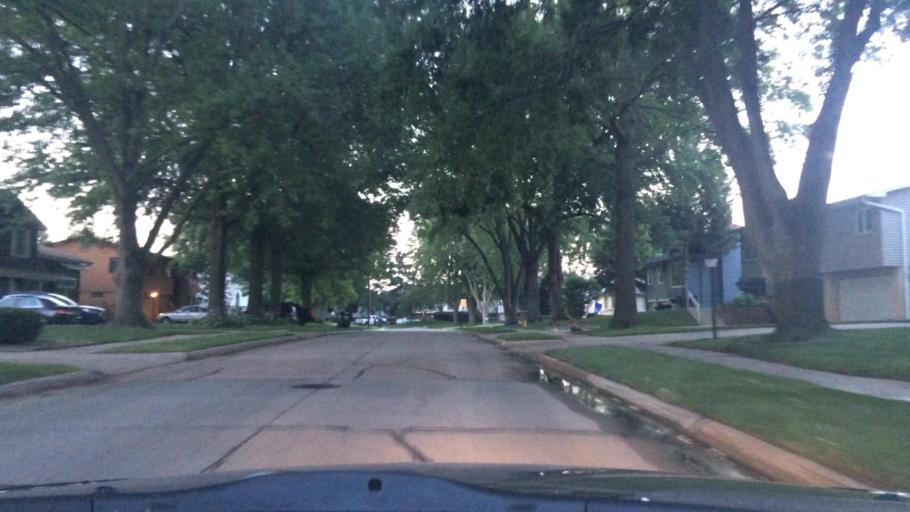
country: US
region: Nebraska
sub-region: Douglas County
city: Ralston
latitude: 41.1895
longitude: -96.0519
